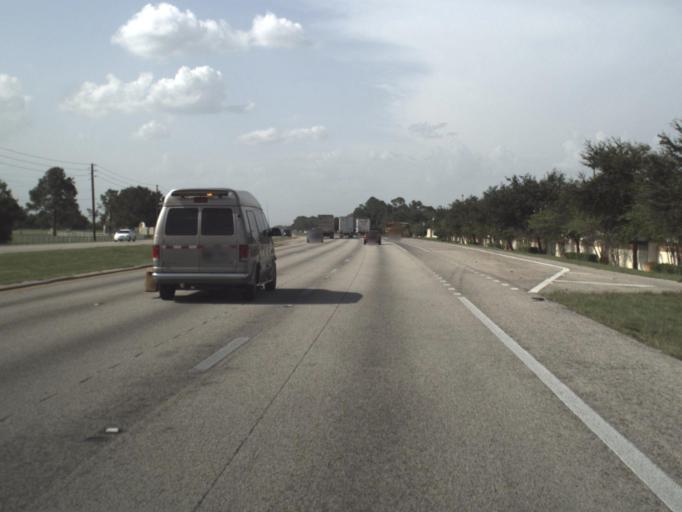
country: US
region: Florida
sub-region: Polk County
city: Lake Wales
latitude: 27.9306
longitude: -81.6081
